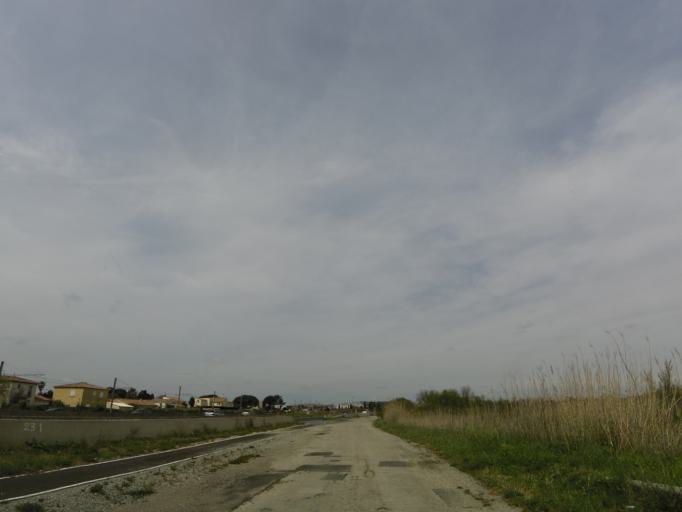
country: FR
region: Languedoc-Roussillon
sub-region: Departement de l'Herault
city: Perols
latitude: 43.5658
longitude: 3.9578
